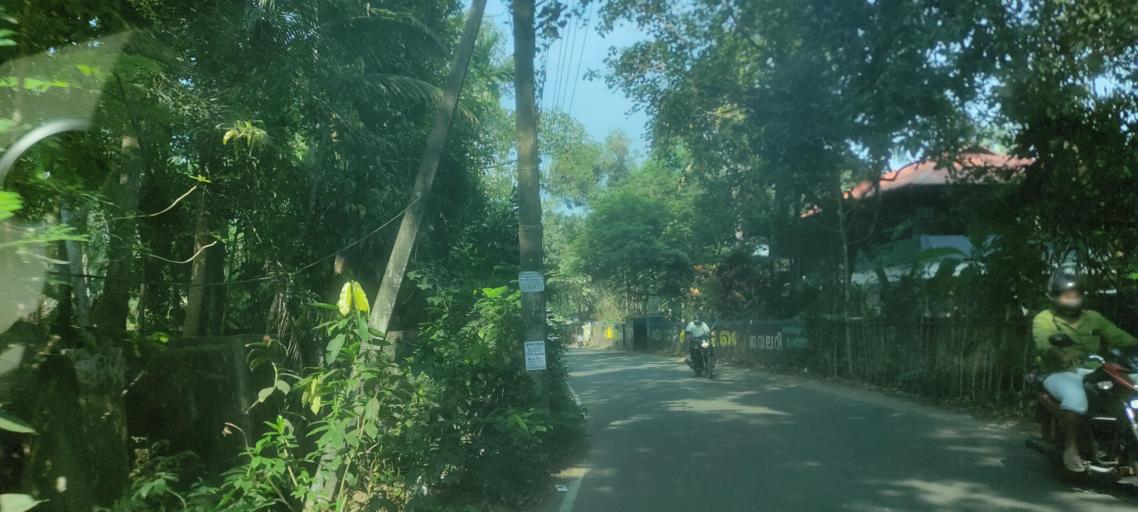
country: IN
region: Kerala
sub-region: Alappuzha
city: Kutiatodu
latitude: 9.7685
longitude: 76.3148
